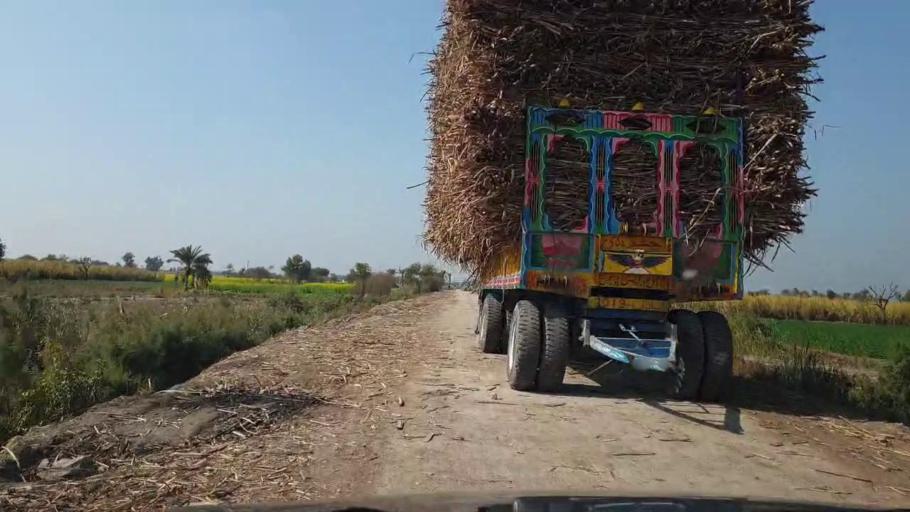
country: PK
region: Sindh
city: Sinjhoro
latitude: 26.0478
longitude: 68.7324
